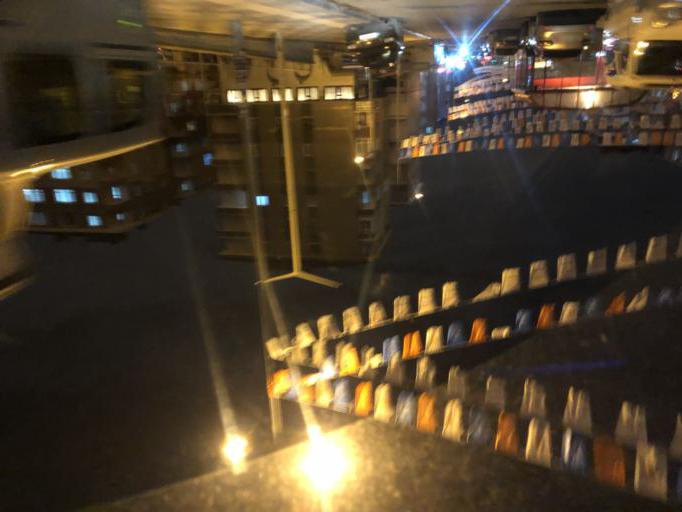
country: TR
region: Ankara
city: Batikent
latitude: 39.9694
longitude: 32.7826
